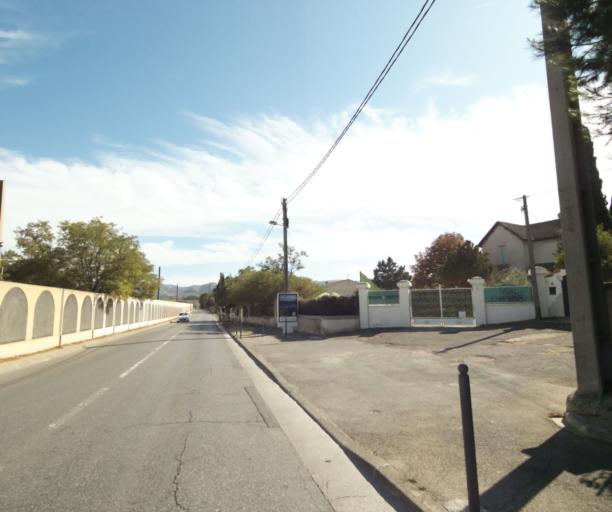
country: FR
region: Provence-Alpes-Cote d'Azur
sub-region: Departement des Bouches-du-Rhone
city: Saint-Victoret
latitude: 43.4087
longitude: 5.2541
